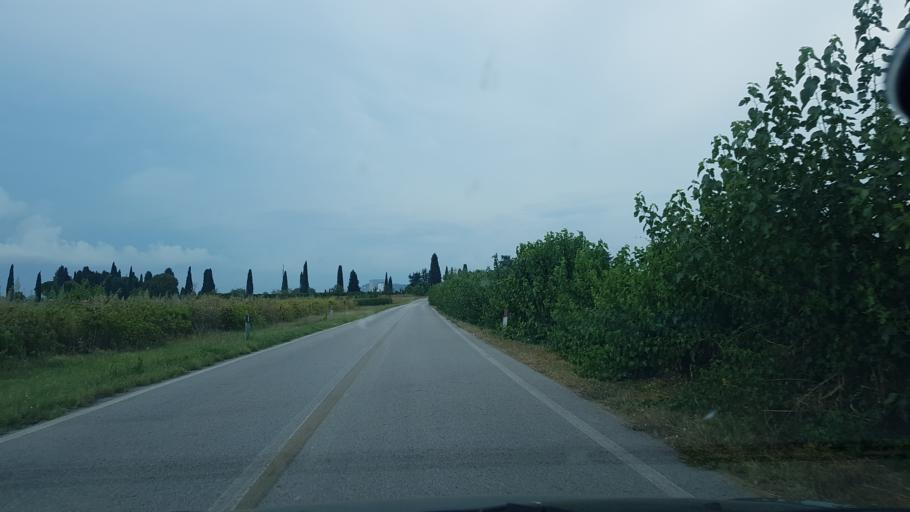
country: IT
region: Friuli Venezia Giulia
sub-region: Provincia di Gorizia
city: Farra d'Isonzo
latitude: 45.9021
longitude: 13.5135
